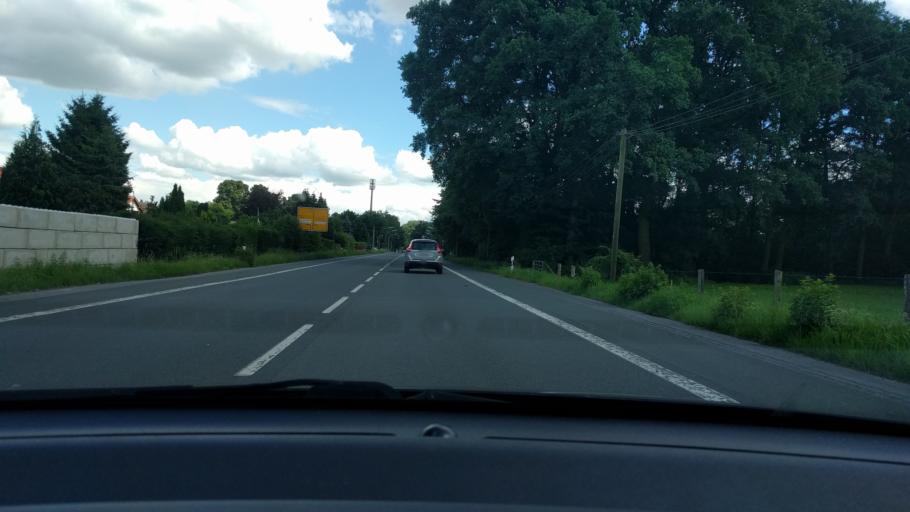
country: DE
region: North Rhine-Westphalia
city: Oer-Erkenschwick
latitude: 51.6999
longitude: 7.3052
